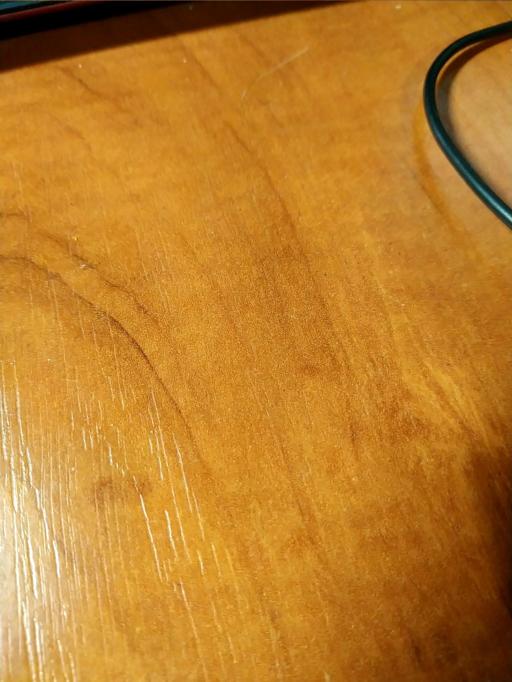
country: RU
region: Smolensk
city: Yartsevo
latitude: 55.4288
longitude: 32.8264
